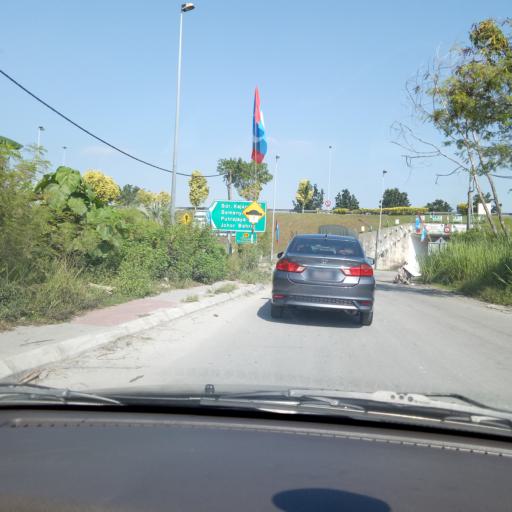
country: MY
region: Selangor
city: Kampong Baharu Balakong
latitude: 3.0138
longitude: 101.7694
